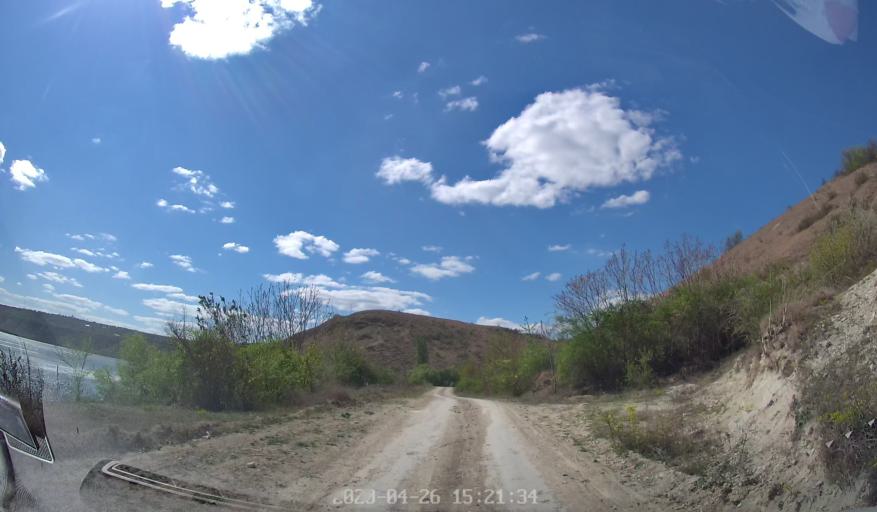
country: MD
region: Telenesti
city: Cocieri
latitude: 47.3645
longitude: 29.0928
